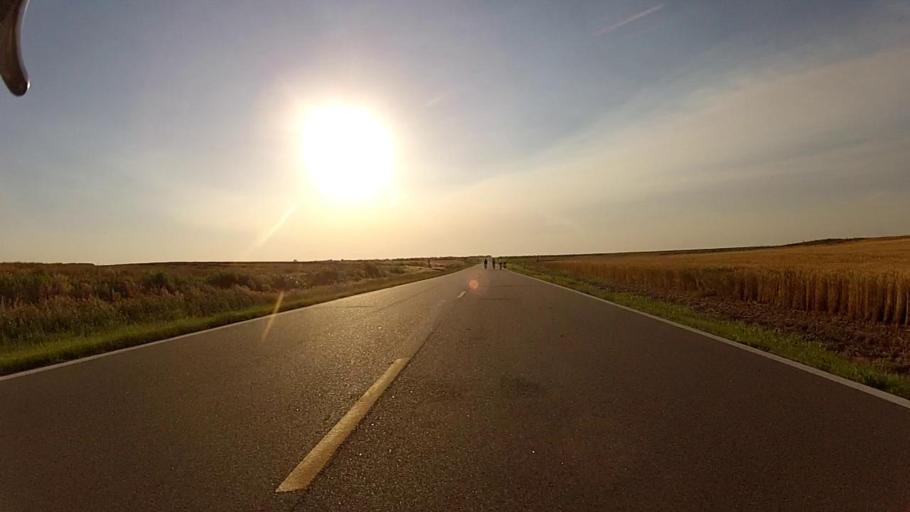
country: US
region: Kansas
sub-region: Harper County
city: Anthony
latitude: 37.1545
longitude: -97.8127
